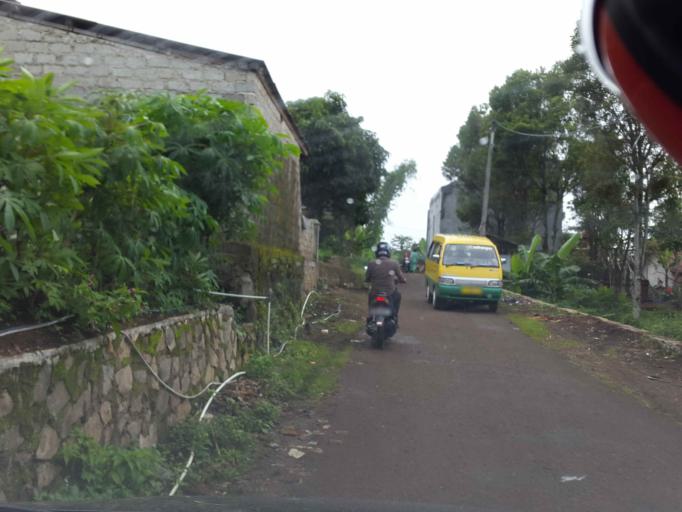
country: ID
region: West Java
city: Padalarang
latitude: -6.8330
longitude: 107.5147
